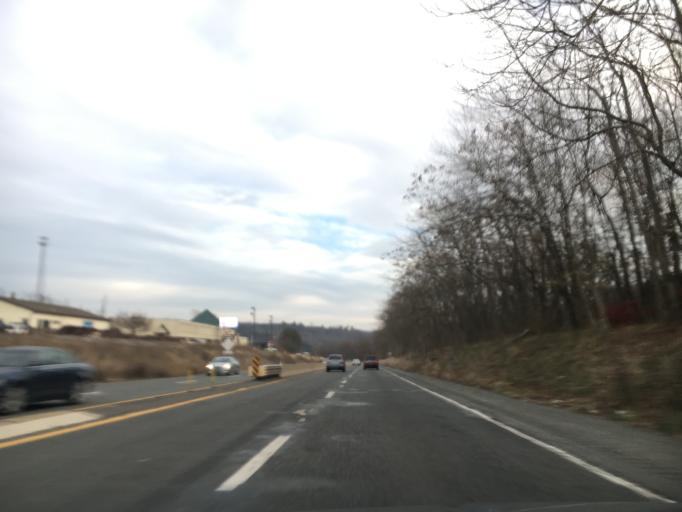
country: US
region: Pennsylvania
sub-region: Carbon County
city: Weissport East
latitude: 40.8217
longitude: -75.6875
